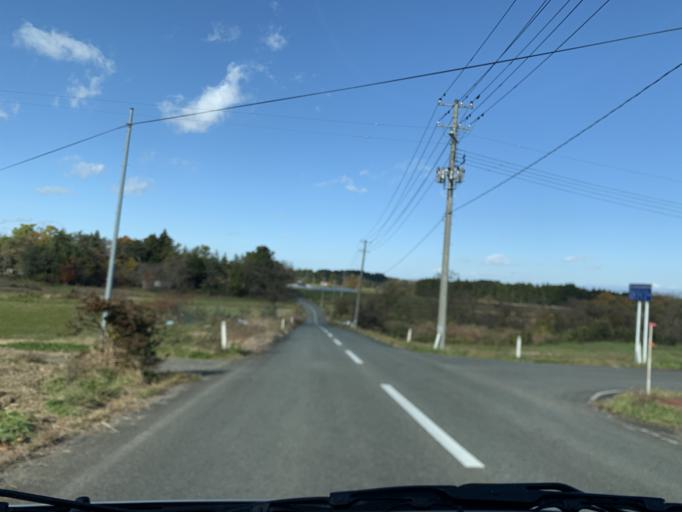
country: JP
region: Iwate
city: Mizusawa
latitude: 39.0638
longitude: 141.1126
